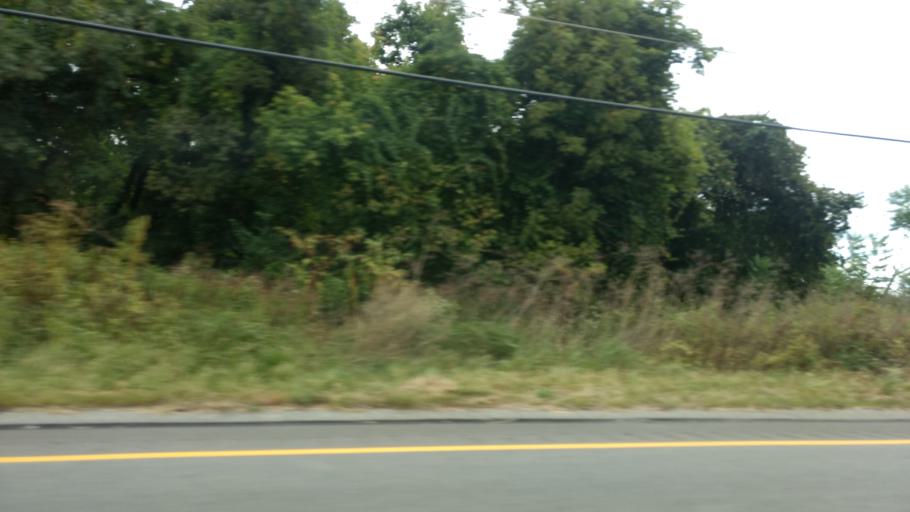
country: US
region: Pennsylvania
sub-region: Westmoreland County
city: Fellsburg
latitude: 40.1989
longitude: -79.8330
